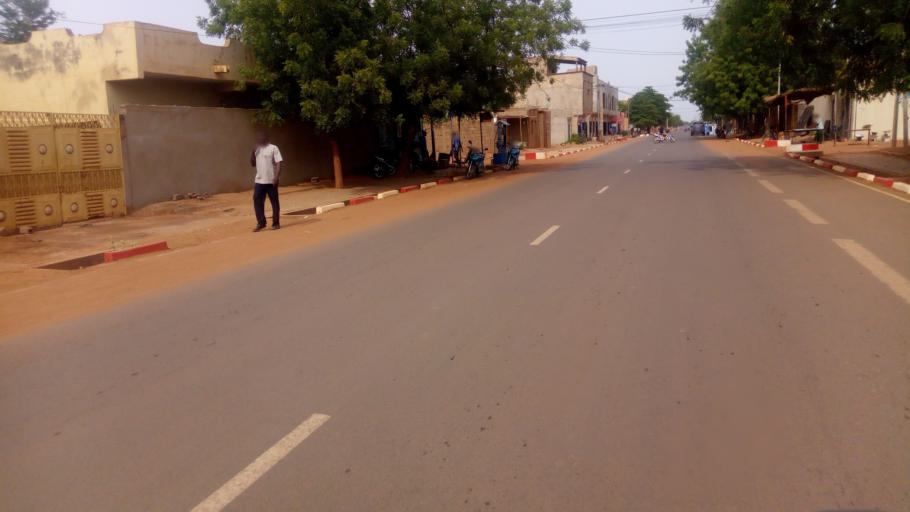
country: ML
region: Segou
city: Segou
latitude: 13.4346
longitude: -6.2684
